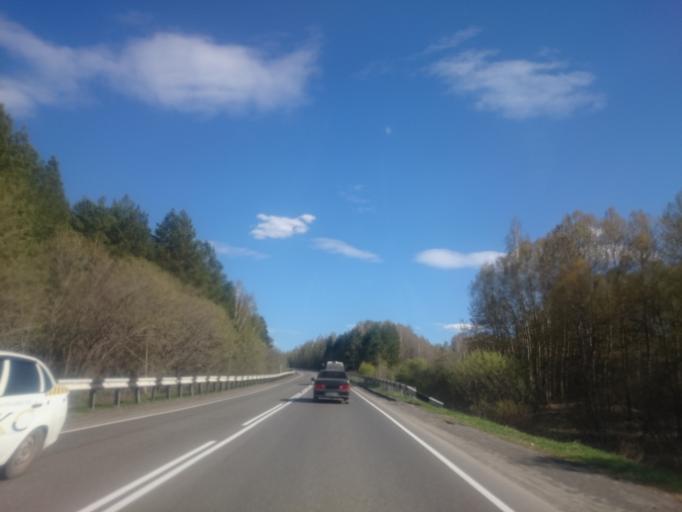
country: RU
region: Sverdlovsk
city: Lesnoy
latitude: 57.6236
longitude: 63.1634
